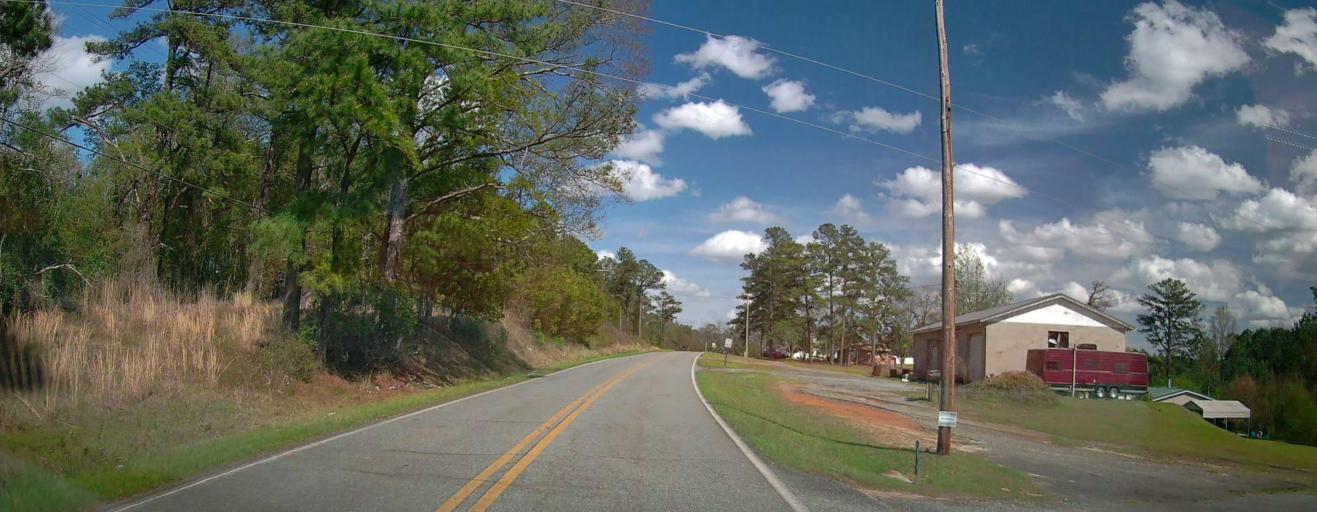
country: US
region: Georgia
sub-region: Bibb County
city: Macon
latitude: 32.8075
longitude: -83.4811
